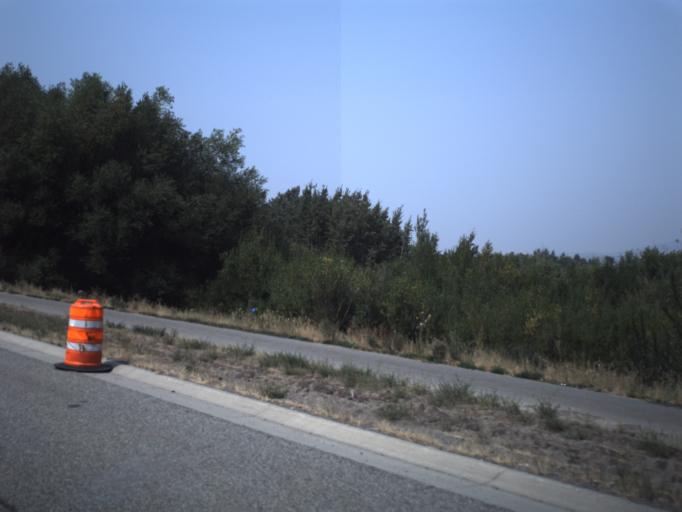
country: US
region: Utah
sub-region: Summit County
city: Snyderville
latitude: 40.6838
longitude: -111.5375
